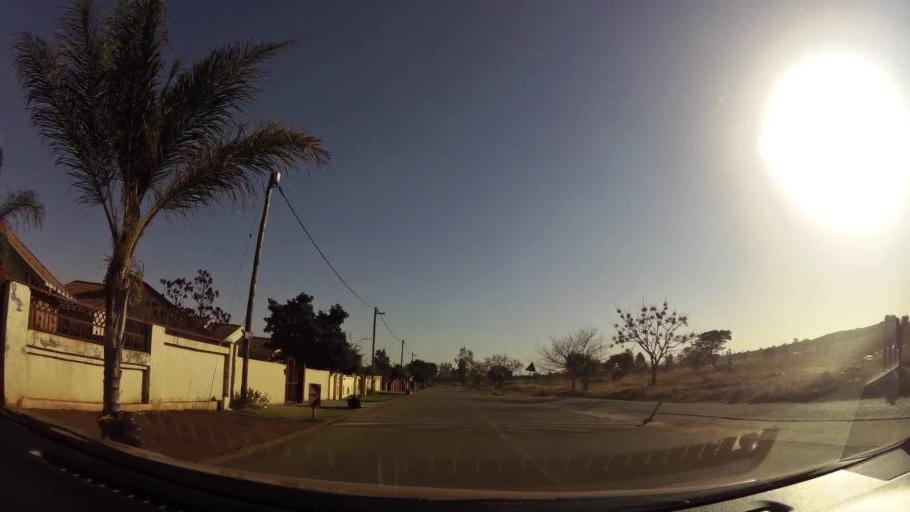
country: ZA
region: Gauteng
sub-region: City of Tshwane Metropolitan Municipality
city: Mabopane
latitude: -25.5833
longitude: 28.1091
